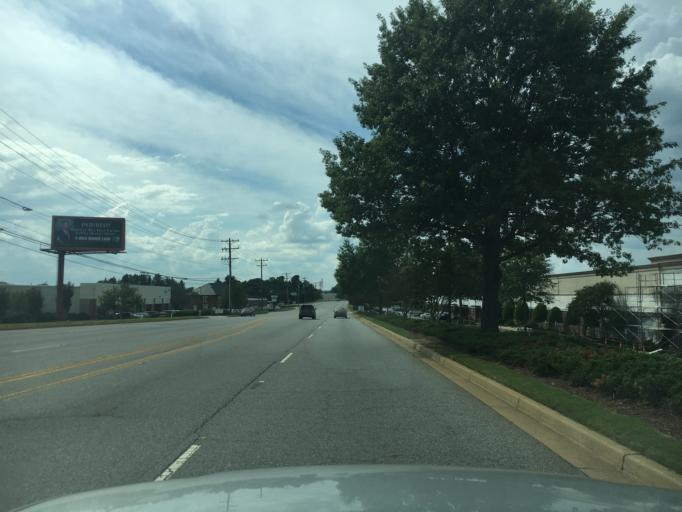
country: US
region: South Carolina
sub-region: Greenville County
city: Five Forks
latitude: 34.8536
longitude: -82.2393
